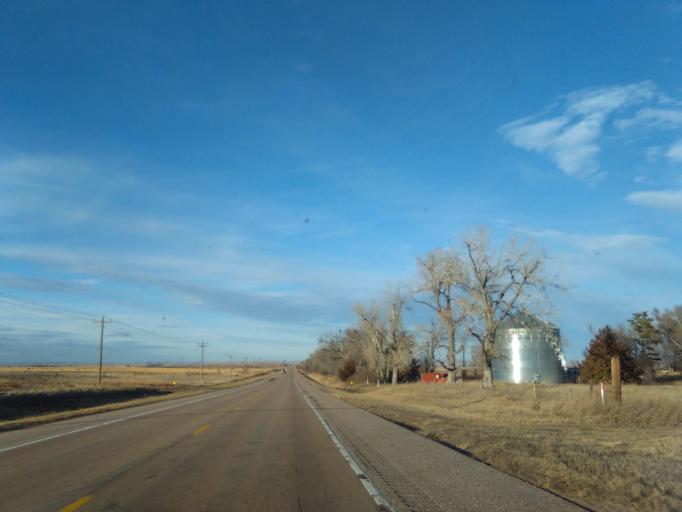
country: US
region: Nebraska
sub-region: Morrill County
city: Bridgeport
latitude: 41.5255
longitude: -102.9843
